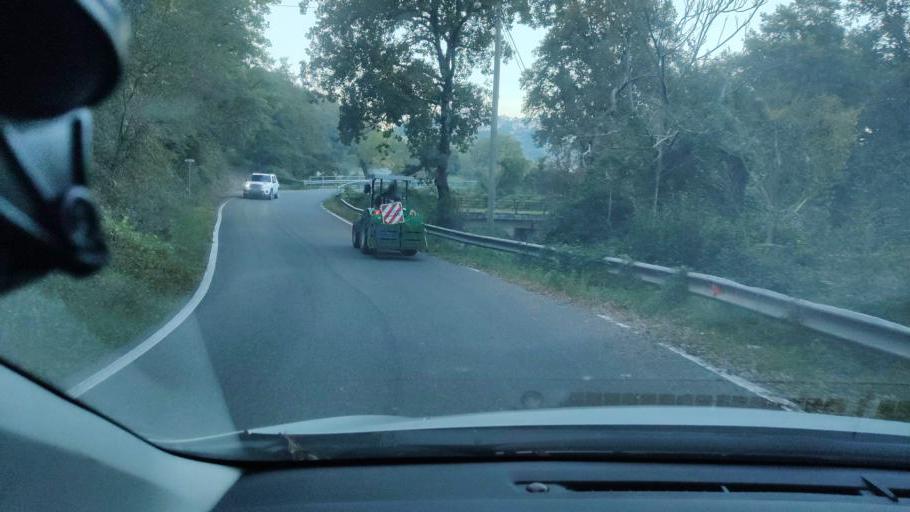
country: IT
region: Umbria
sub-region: Provincia di Terni
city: Amelia
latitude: 42.5907
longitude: 12.4349
